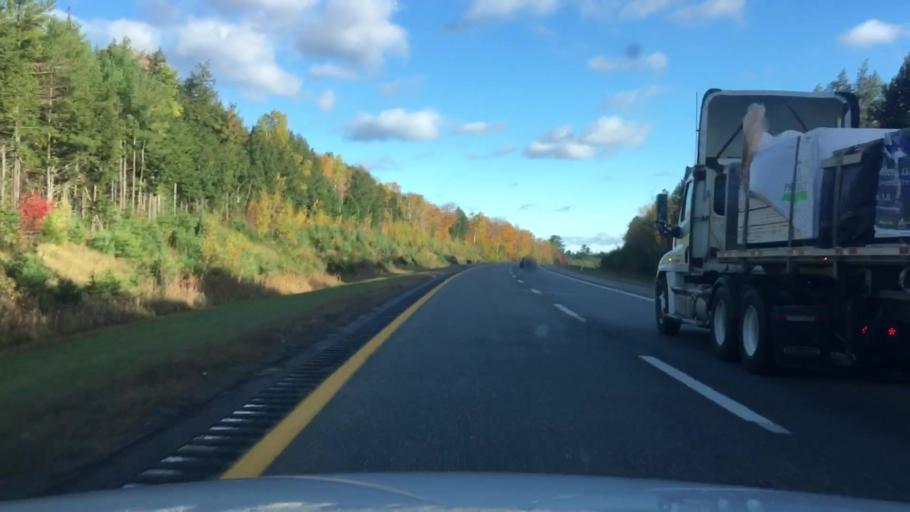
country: US
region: Maine
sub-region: Penobscot County
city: Greenbush
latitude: 45.1527
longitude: -68.7039
